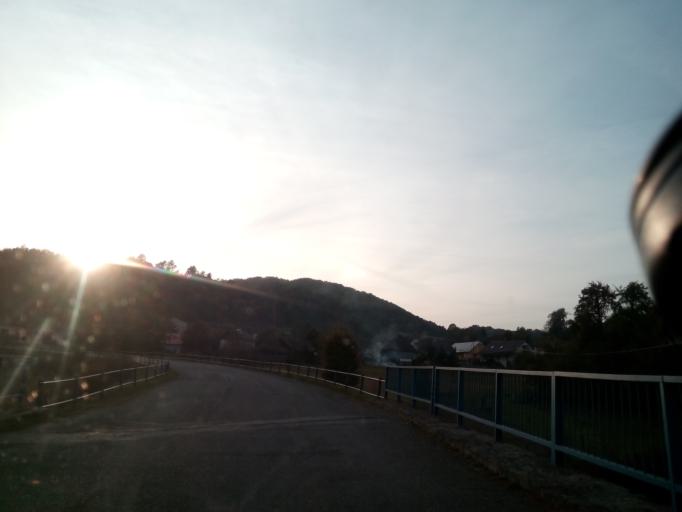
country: SK
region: Presovsky
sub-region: Okres Bardejov
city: Bardejov
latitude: 49.3599
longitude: 21.3989
